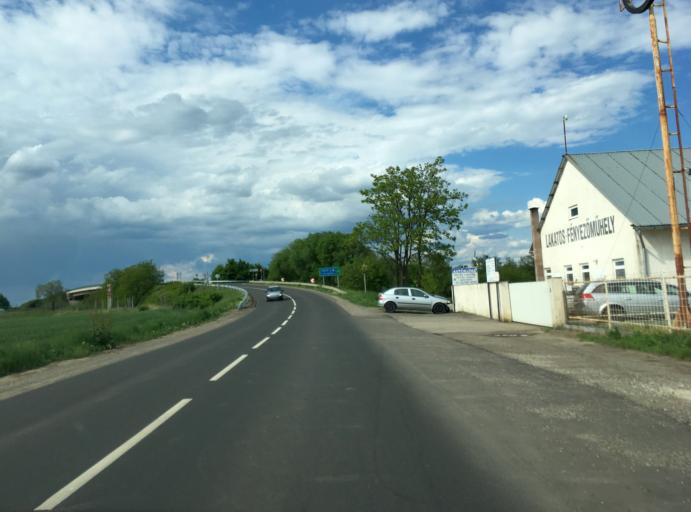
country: HU
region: Heves
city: Hered
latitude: 47.6650
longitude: 19.6212
